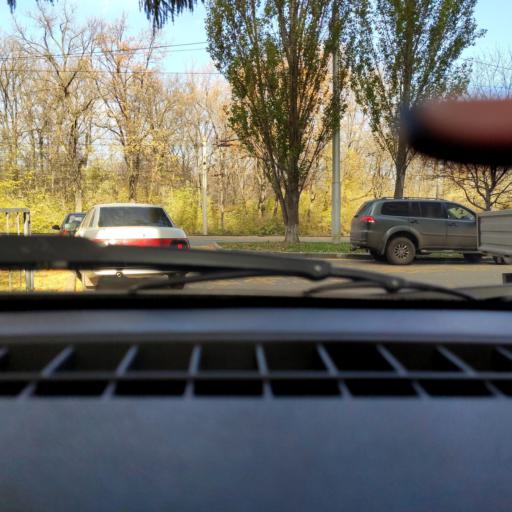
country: RU
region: Bashkortostan
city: Ufa
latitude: 54.7965
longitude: 56.0533
